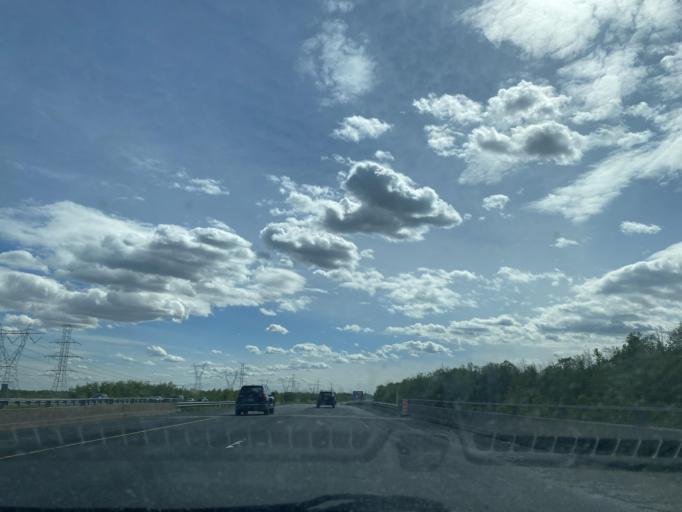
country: CA
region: Quebec
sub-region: Monteregie
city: Brossard
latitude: 45.4687
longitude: -73.3940
